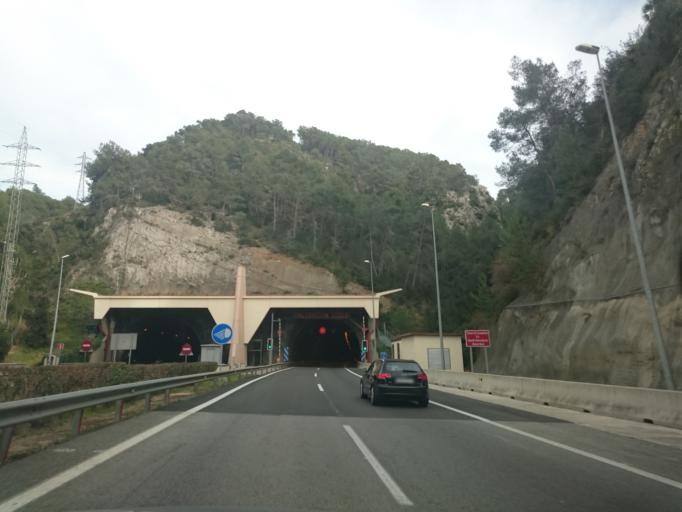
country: ES
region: Catalonia
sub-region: Provincia de Barcelona
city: Sitges
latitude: 41.2501
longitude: 1.8696
